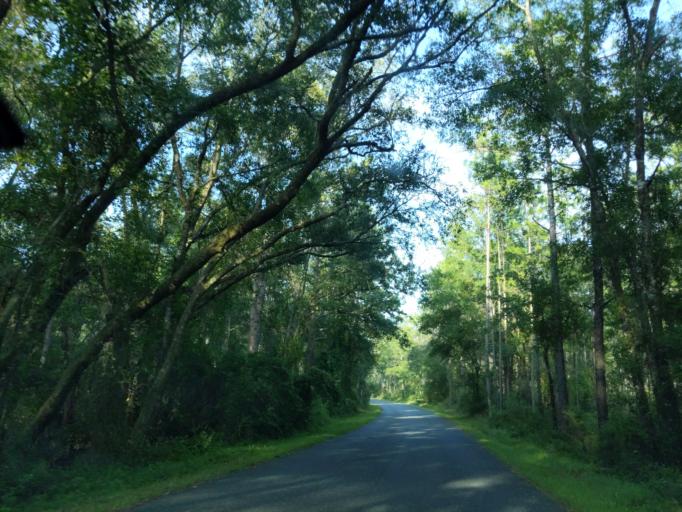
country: US
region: Florida
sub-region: Leon County
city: Woodville
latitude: 30.3463
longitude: -84.3743
